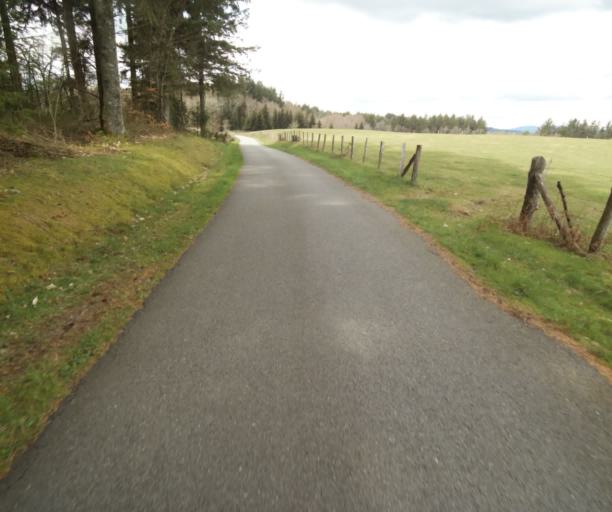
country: FR
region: Limousin
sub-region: Departement de la Correze
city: Egletons
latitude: 45.3394
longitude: 1.9756
